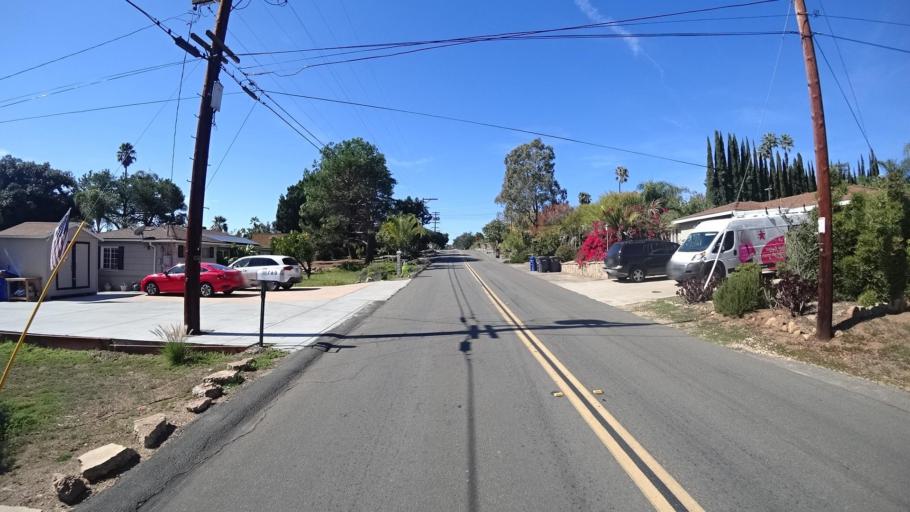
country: US
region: California
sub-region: San Diego County
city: Casa de Oro-Mount Helix
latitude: 32.7556
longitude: -116.9634
